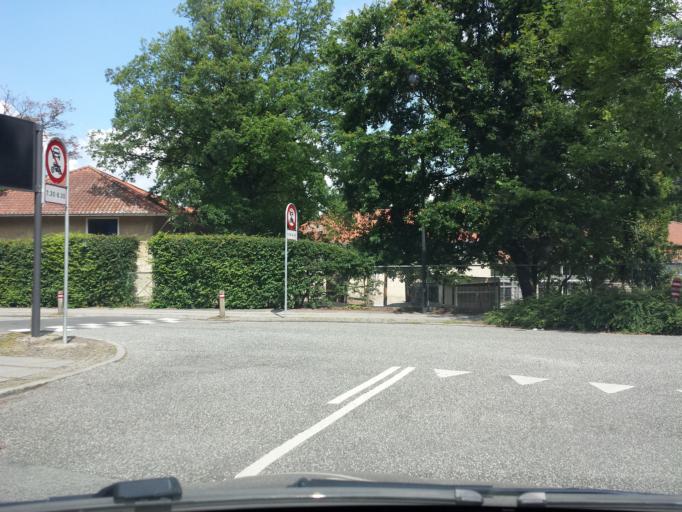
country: DK
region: Capital Region
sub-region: Gentofte Kommune
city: Charlottenlund
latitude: 55.7652
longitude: 12.5700
